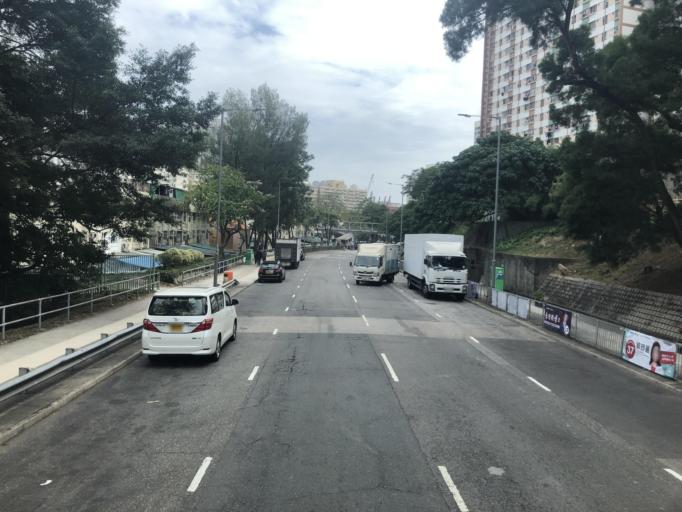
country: HK
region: Tsuen Wan
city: Tsuen Wan
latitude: 22.3509
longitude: 114.1038
